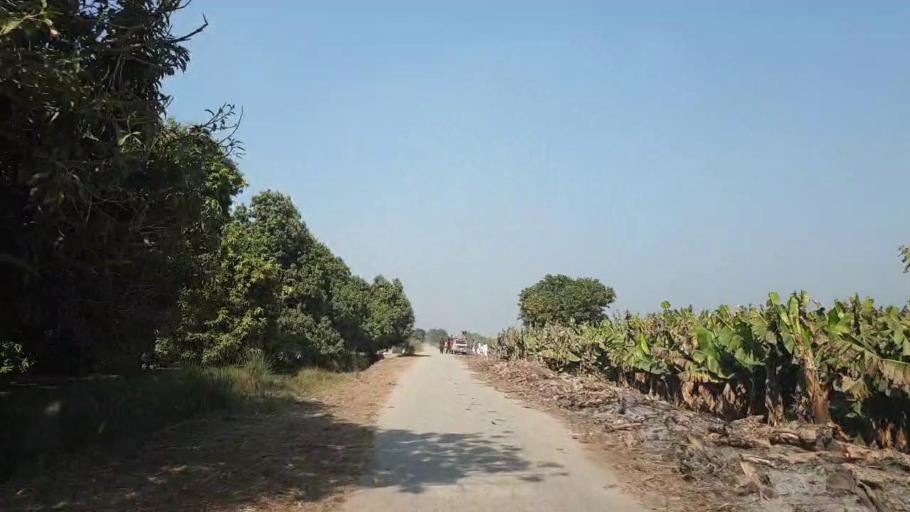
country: PK
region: Sindh
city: Tando Allahyar
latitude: 25.5055
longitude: 68.8221
